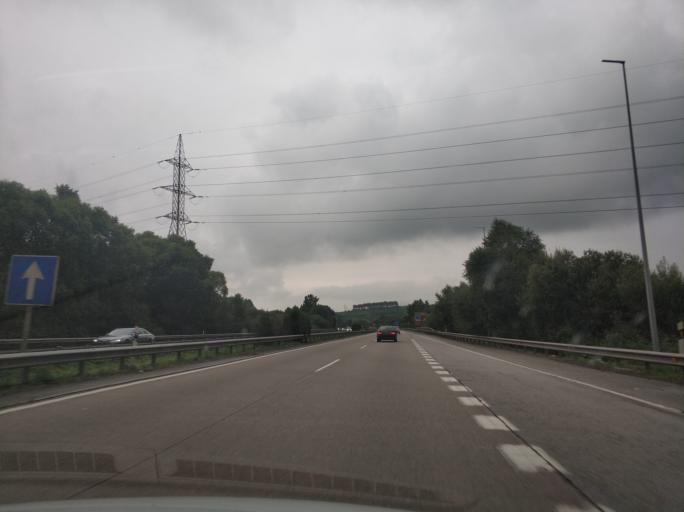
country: ES
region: Asturias
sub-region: Province of Asturias
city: Corvera de Asturias
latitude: 43.5192
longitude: -5.8223
